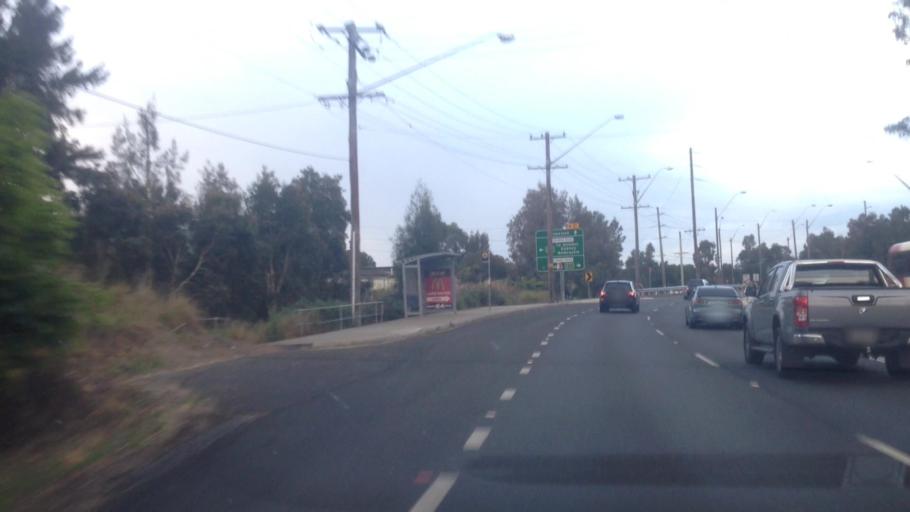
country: AU
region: New South Wales
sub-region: Wyong Shire
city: Kanwal
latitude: -33.2534
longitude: 151.4881
